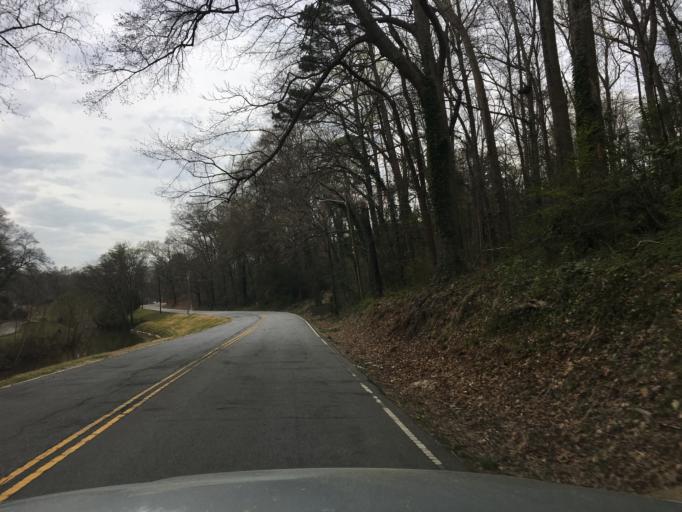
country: US
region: South Carolina
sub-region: Greenville County
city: Greenville
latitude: 34.8439
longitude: -82.3897
